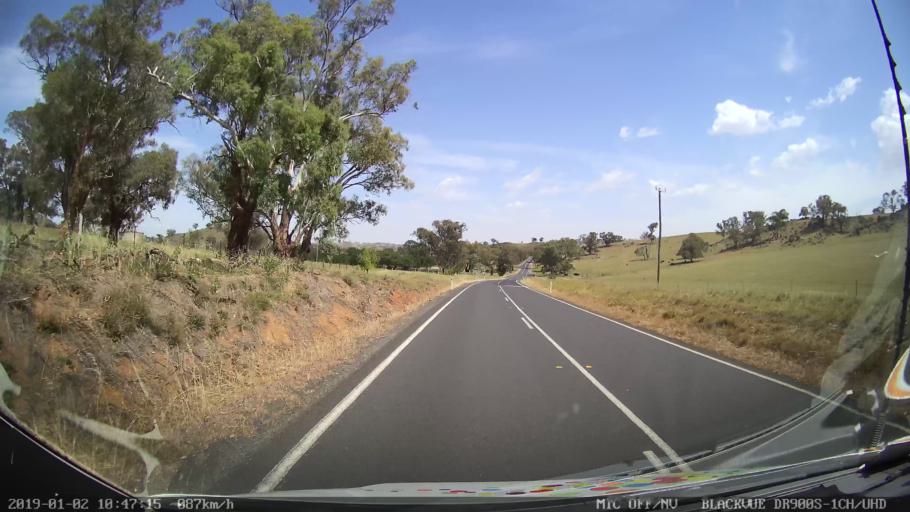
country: AU
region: New South Wales
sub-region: Cootamundra
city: Cootamundra
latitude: -34.7469
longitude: 148.2752
